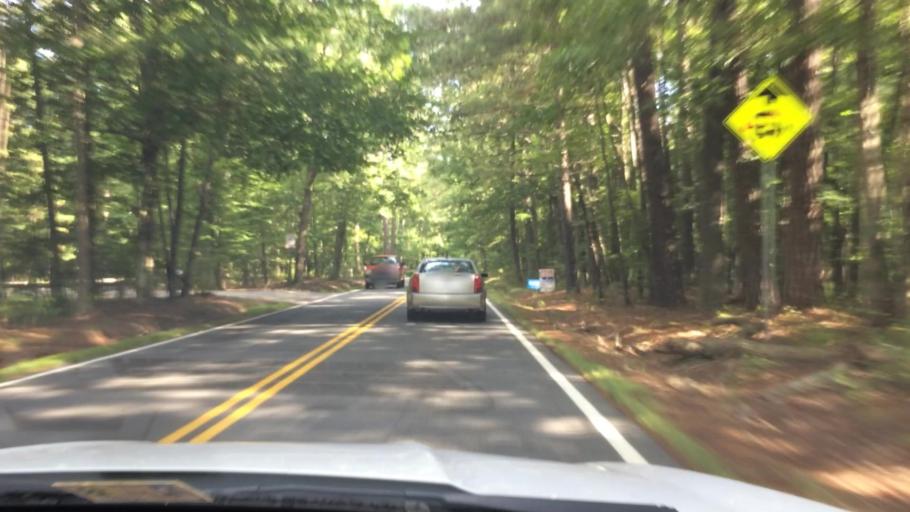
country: US
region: Virginia
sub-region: King William County
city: West Point
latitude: 37.5021
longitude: -76.8217
